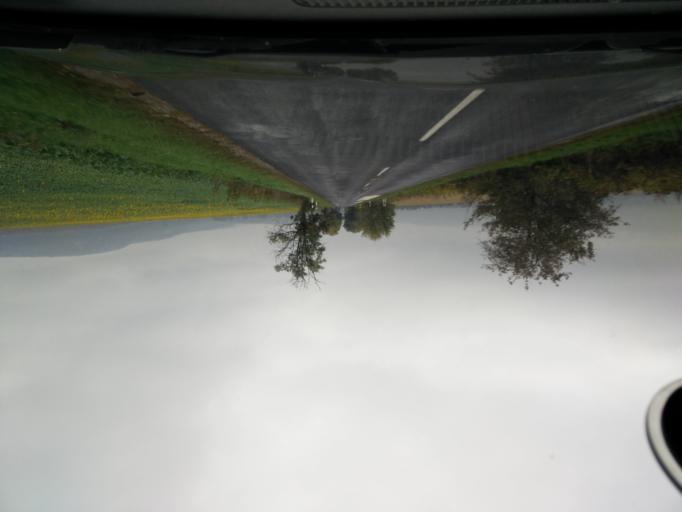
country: HU
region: Komarom-Esztergom
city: Tarjan
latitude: 47.6250
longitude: 18.5160
